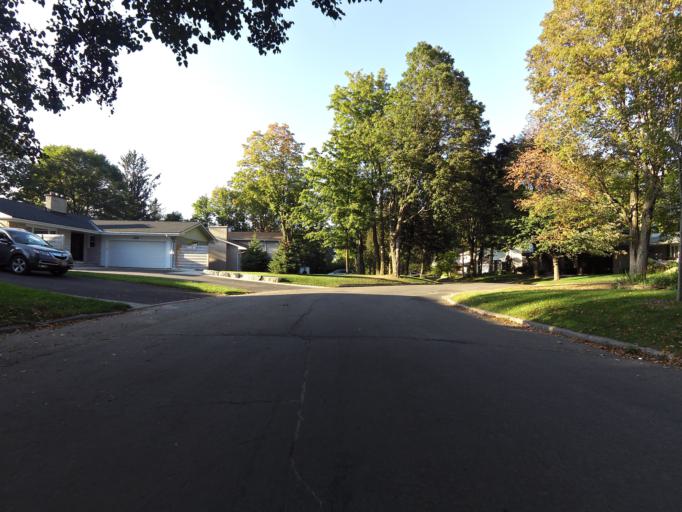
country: CA
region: Ontario
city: Ottawa
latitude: 45.3869
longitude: -75.6651
